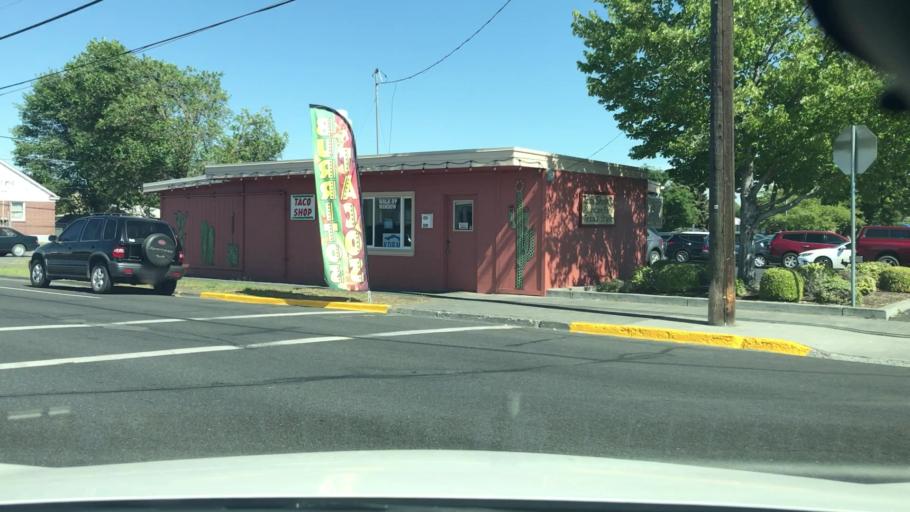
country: US
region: Washington
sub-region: Grant County
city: Moses Lake
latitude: 47.1275
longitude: -119.2809
